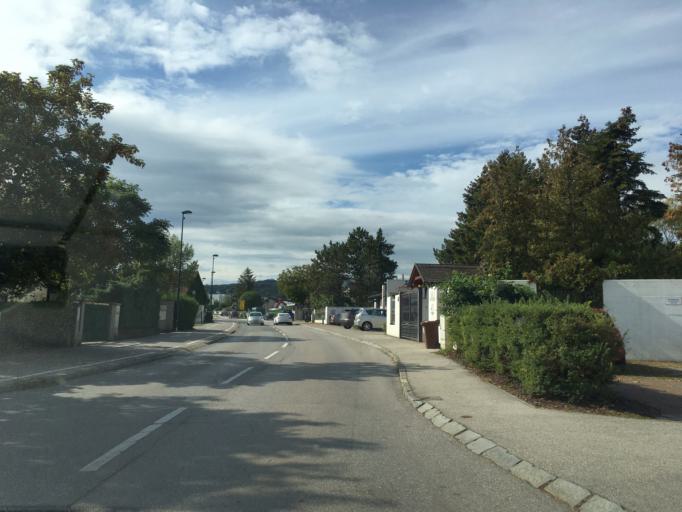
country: AT
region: Lower Austria
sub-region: Politischer Bezirk Modling
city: Maria Enzersdorf
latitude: 48.0988
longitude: 16.2957
